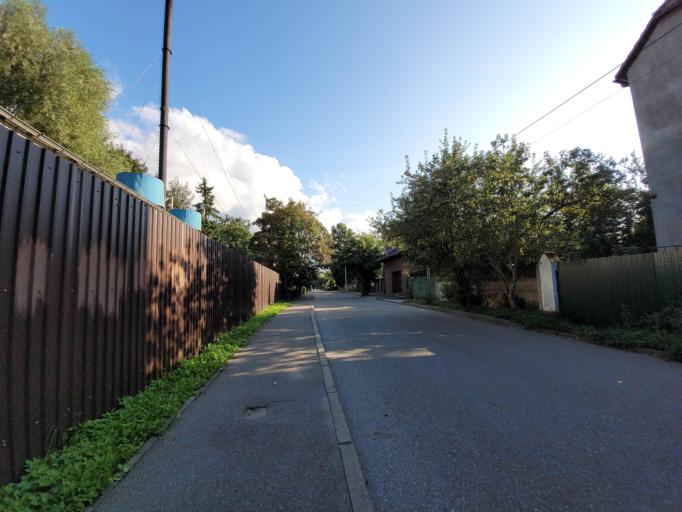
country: RU
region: Kaliningrad
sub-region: Gorod Kaliningrad
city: Kaliningrad
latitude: 54.7202
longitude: 20.4588
